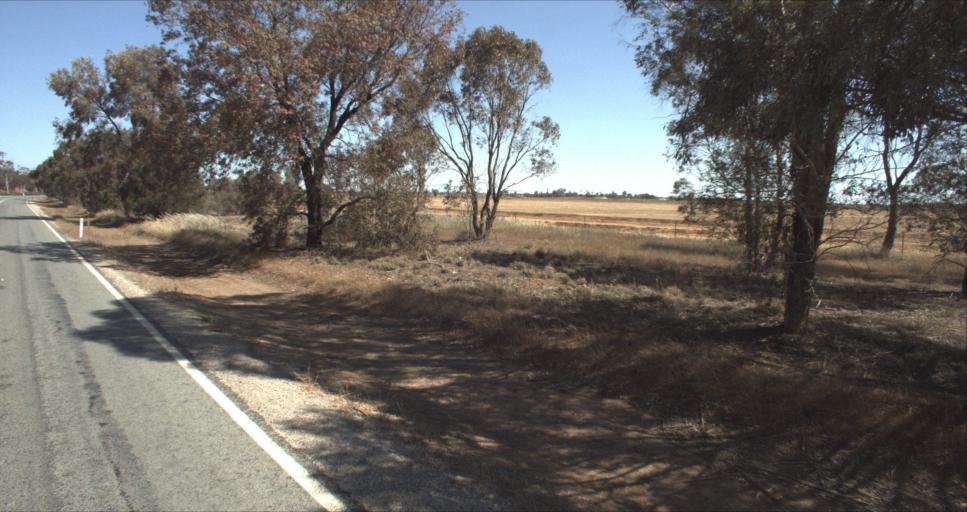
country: AU
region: New South Wales
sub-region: Leeton
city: Leeton
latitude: -34.4952
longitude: 146.4328
